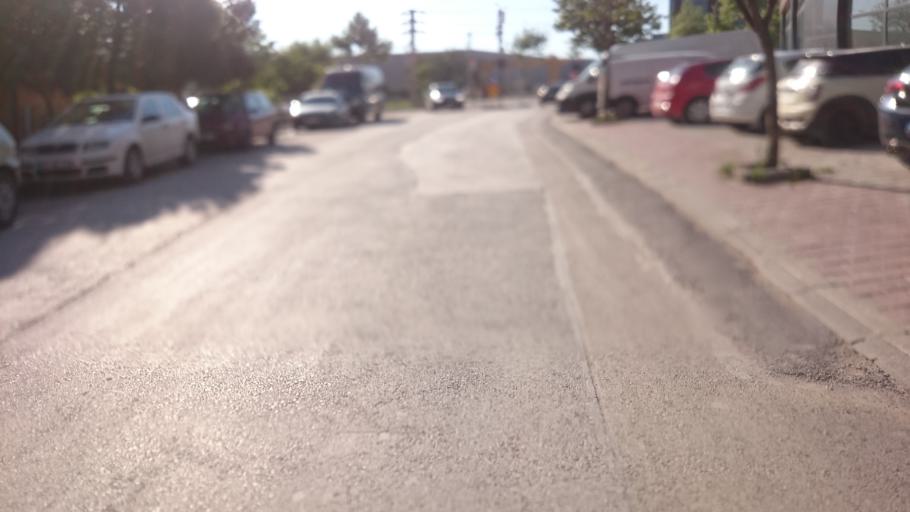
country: TR
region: Bursa
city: Niluefer
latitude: 40.2248
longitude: 28.9602
